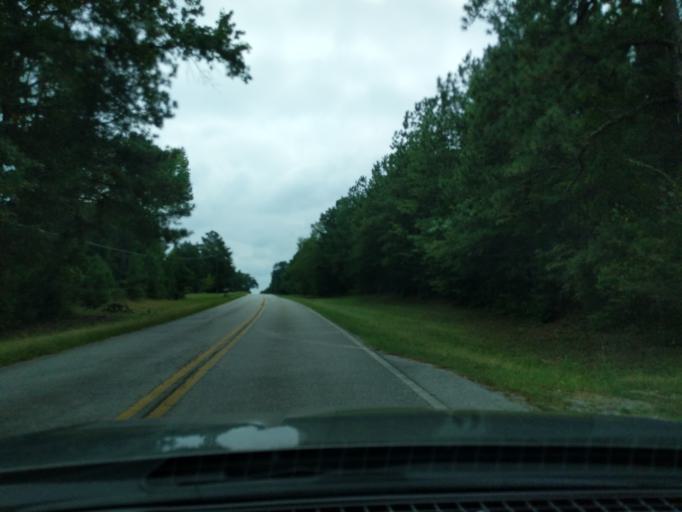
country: US
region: Georgia
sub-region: Columbia County
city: Appling
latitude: 33.5963
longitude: -82.3860
